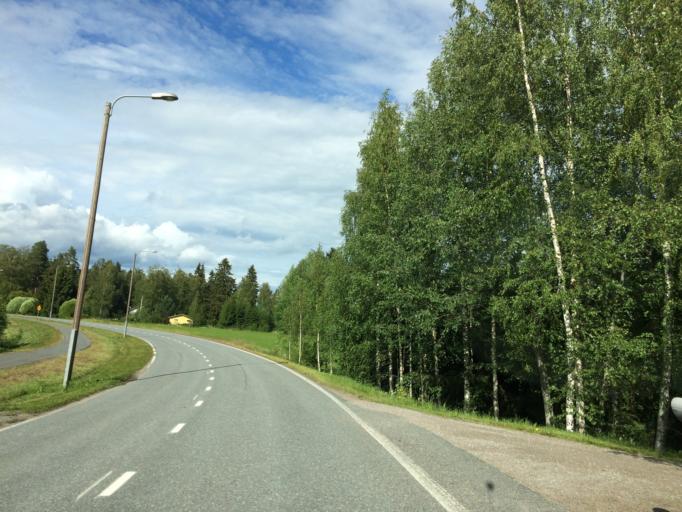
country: FI
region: Haeme
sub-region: Haemeenlinna
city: Janakkala
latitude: 60.9057
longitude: 24.6112
